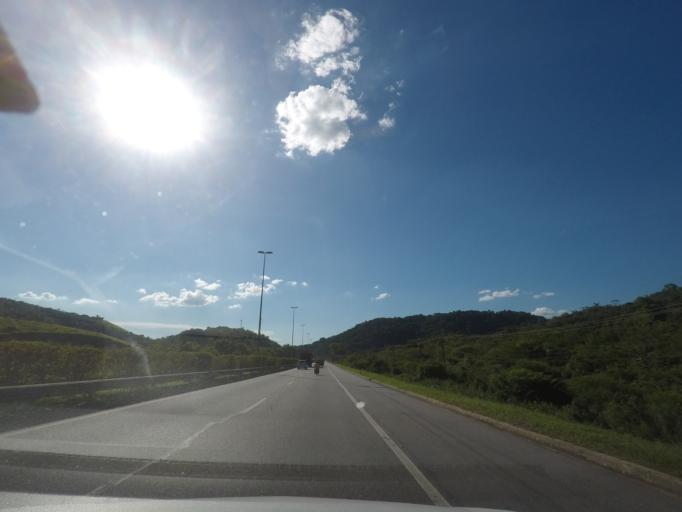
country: BR
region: Rio de Janeiro
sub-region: Petropolis
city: Petropolis
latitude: -22.6563
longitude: -43.1367
